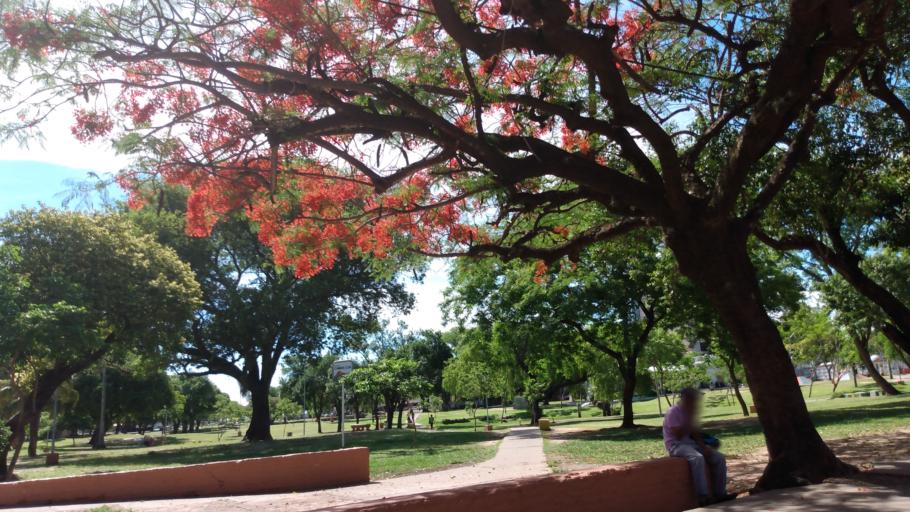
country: AR
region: Corrientes
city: Corrientes
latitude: -27.4659
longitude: -58.8429
